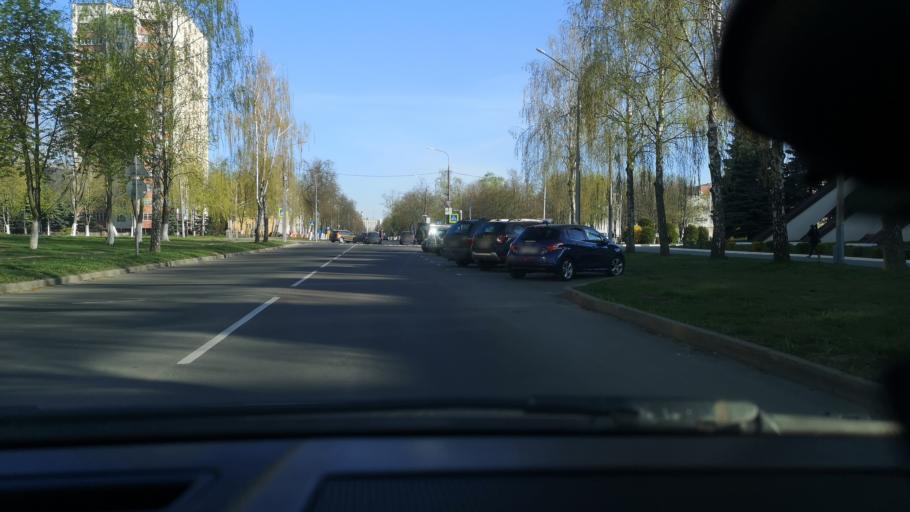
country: BY
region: Gomel
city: Gomel
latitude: 52.4520
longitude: 31.0065
